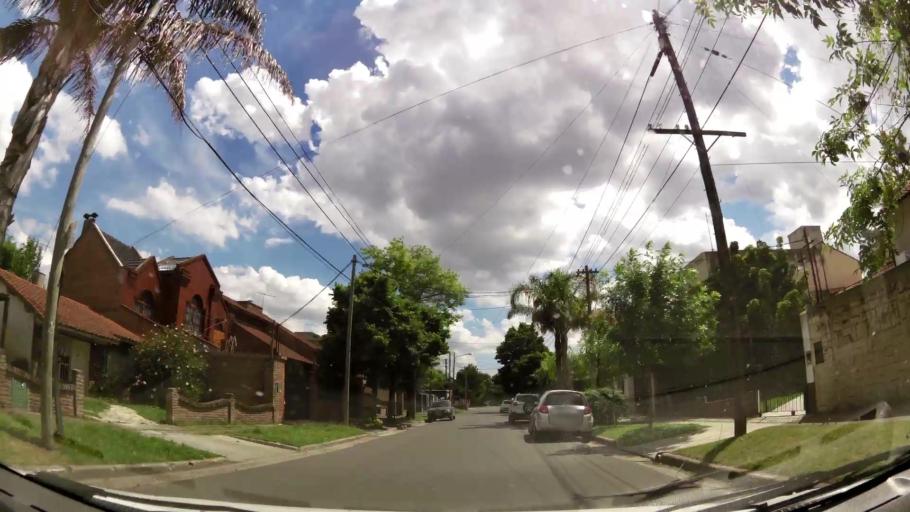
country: AR
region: Buenos Aires
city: Ituzaingo
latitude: -34.6482
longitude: -58.6732
